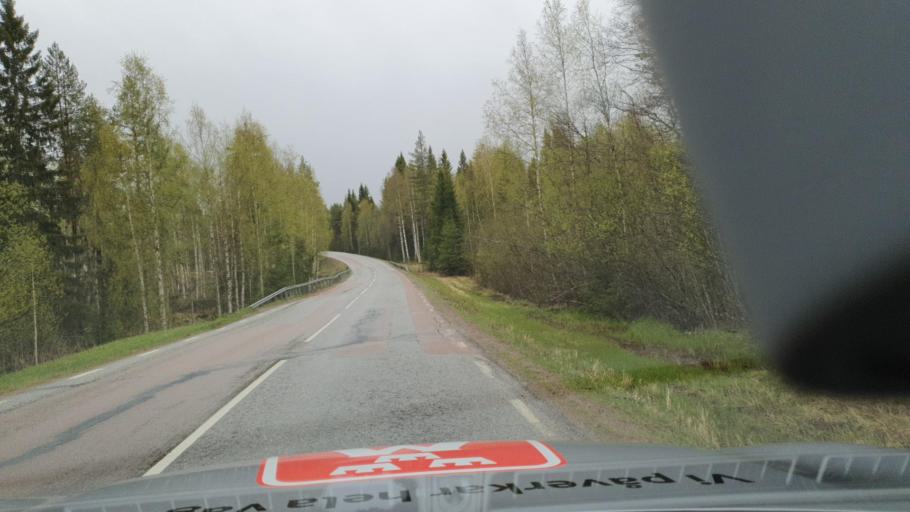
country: SE
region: Vaesternorrland
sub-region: Solleftea Kommun
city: As
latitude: 63.6800
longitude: 16.9951
